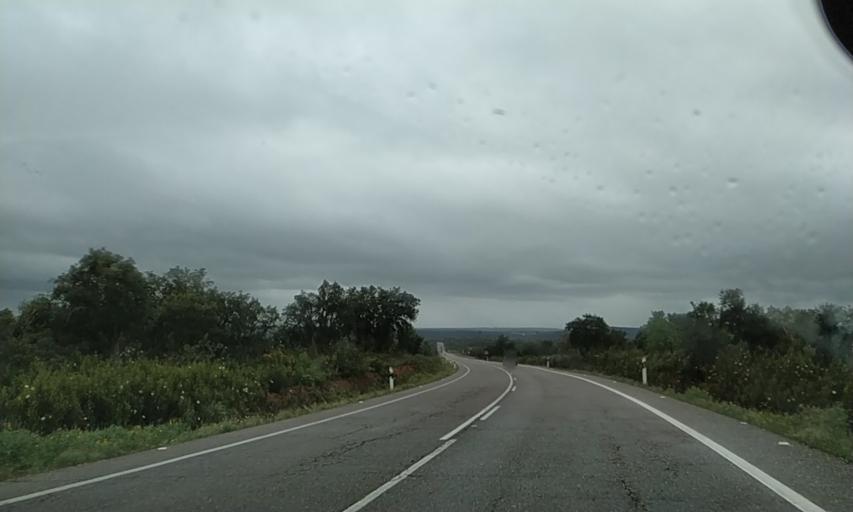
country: ES
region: Extremadura
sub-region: Provincia de Badajoz
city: Puebla de Obando
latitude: 39.1629
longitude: -6.6401
